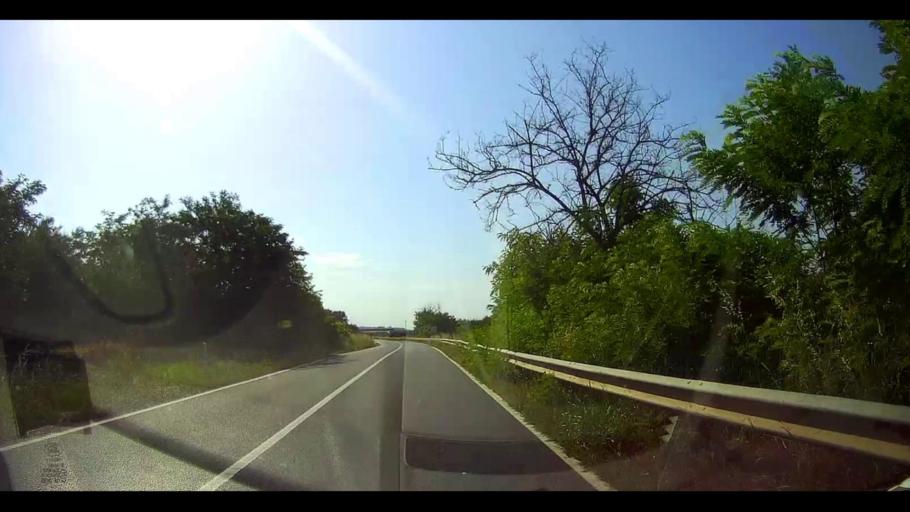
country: IT
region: Calabria
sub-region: Provincia di Crotone
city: Torretta
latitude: 39.4779
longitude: 16.9987
